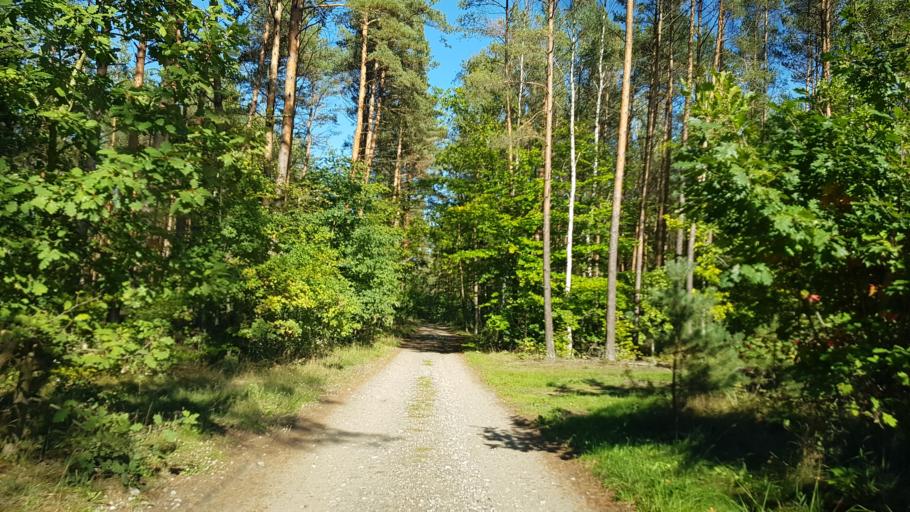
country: PL
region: Lubusz
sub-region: Powiat gorzowski
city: Lubiszyn
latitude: 52.8450
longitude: 14.9343
